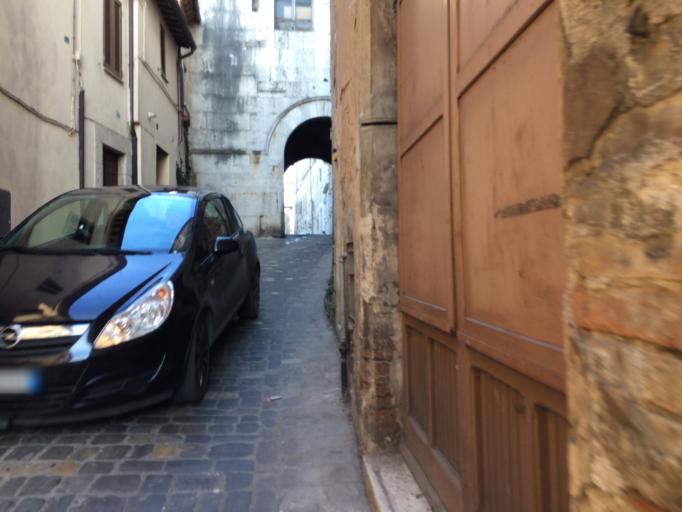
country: IT
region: Umbria
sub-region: Provincia di Terni
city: Amelia
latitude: 42.5561
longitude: 12.4134
